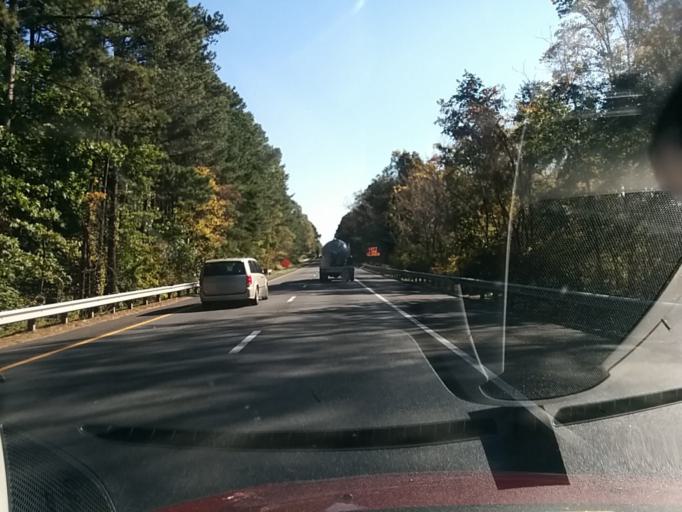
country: US
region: Virginia
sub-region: Albemarle County
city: Crozet
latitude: 38.0334
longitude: -78.6309
